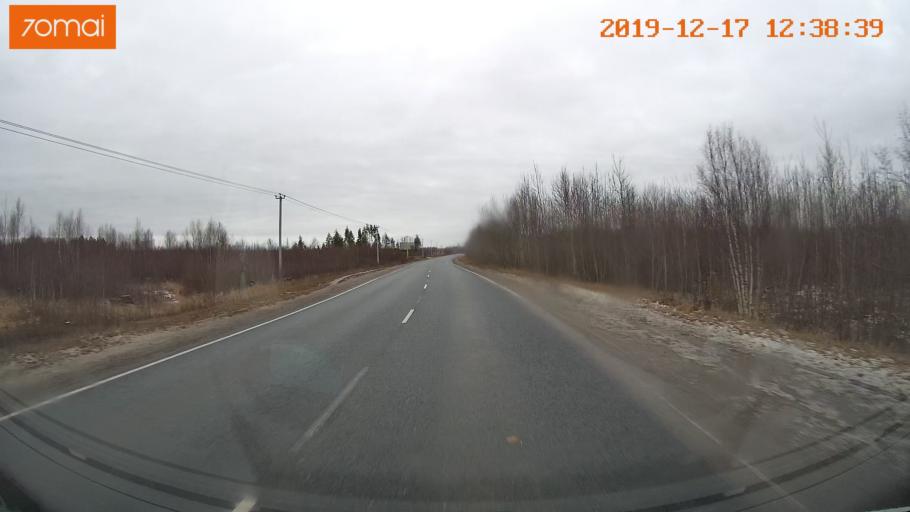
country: RU
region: Moskovskaya
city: Radovitskiy
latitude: 54.9766
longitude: 39.9513
